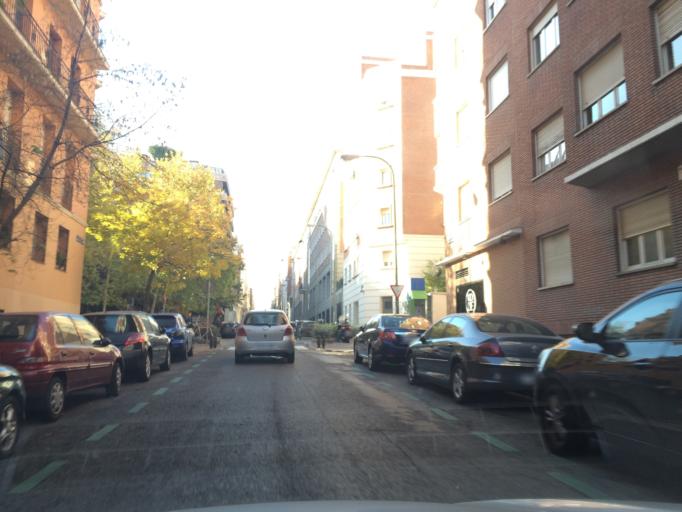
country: ES
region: Madrid
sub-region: Provincia de Madrid
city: Chamberi
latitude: 40.4393
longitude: -3.6940
